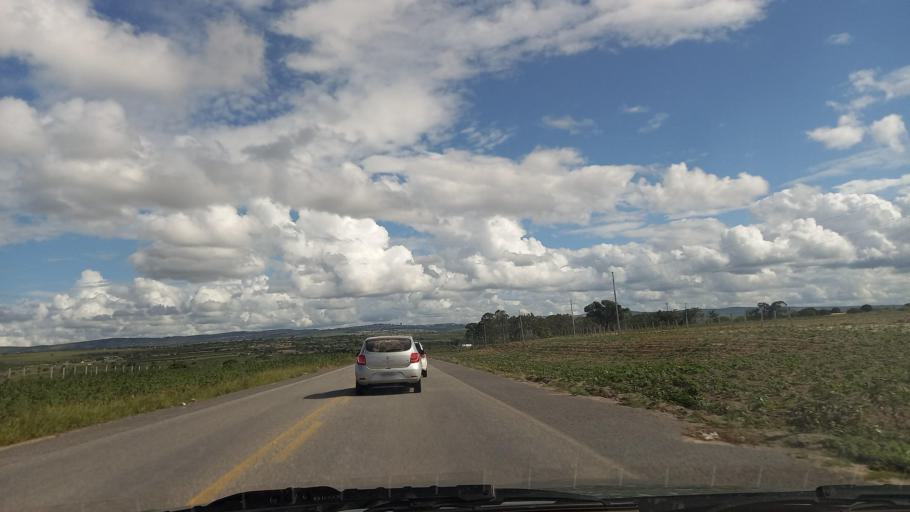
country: BR
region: Pernambuco
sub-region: Sao Joao
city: Sao Joao
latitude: -8.7867
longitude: -36.4329
